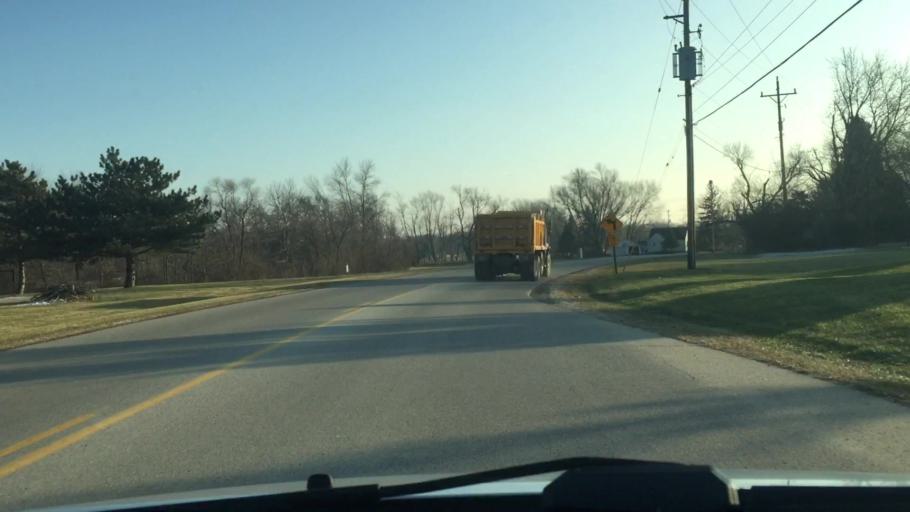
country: US
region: Wisconsin
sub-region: Waukesha County
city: Dousman
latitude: 43.0271
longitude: -88.4784
